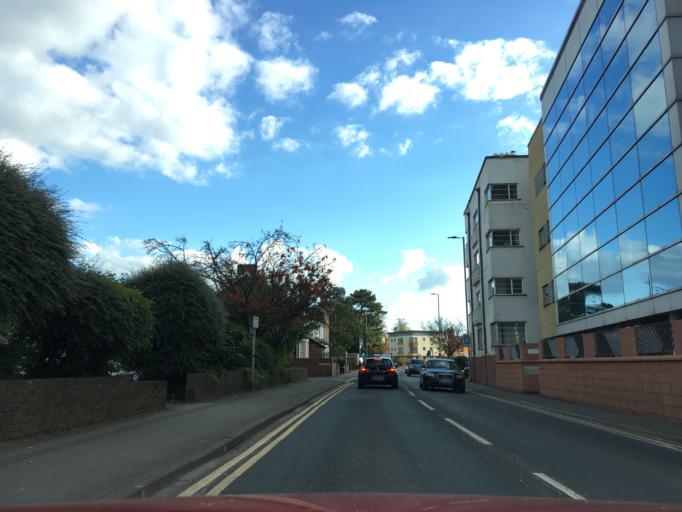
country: GB
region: England
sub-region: Herefordshire
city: Hereford
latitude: 52.0560
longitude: -2.7104
